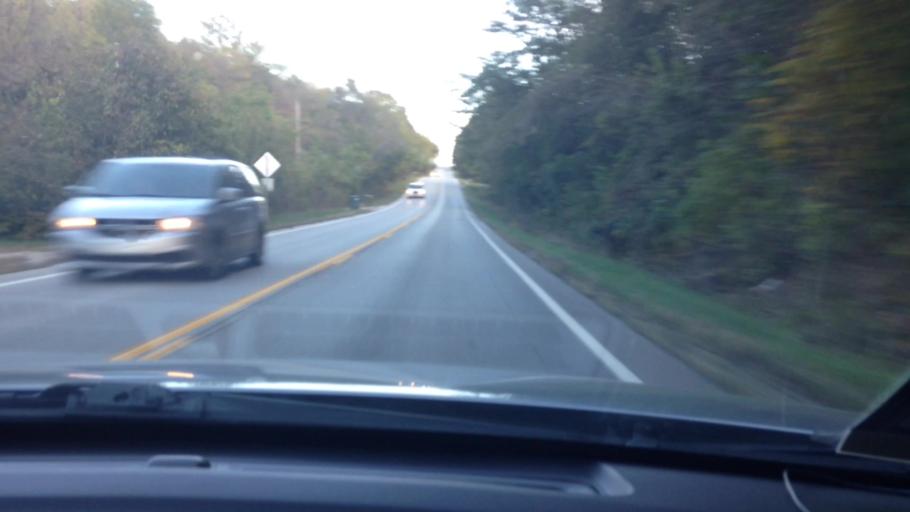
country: US
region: Missouri
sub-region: Platte County
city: Weatherby Lake
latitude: 39.2361
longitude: -94.7972
